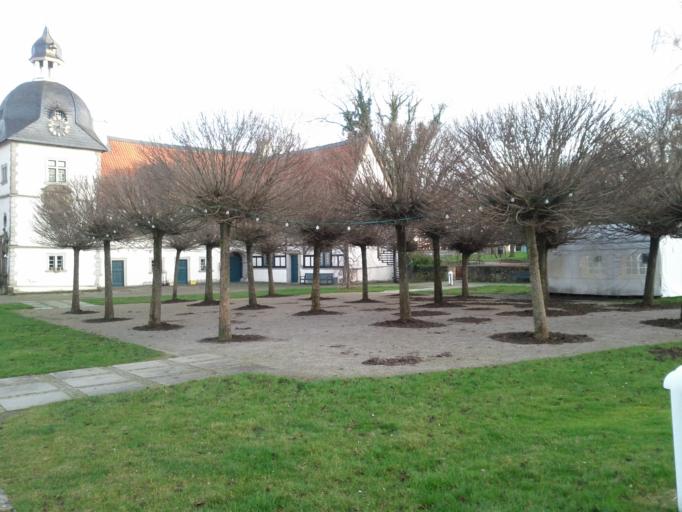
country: DE
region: North Rhine-Westphalia
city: Schwerte
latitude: 51.4930
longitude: 7.5536
